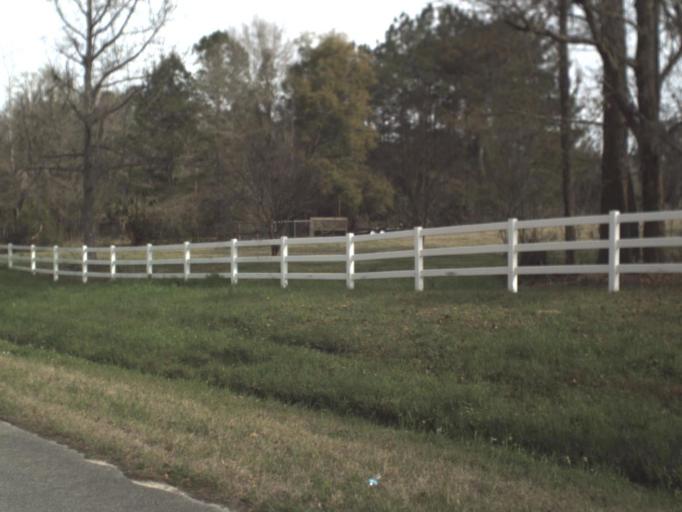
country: US
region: Florida
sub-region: Jefferson County
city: Monticello
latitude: 30.5327
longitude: -83.9533
